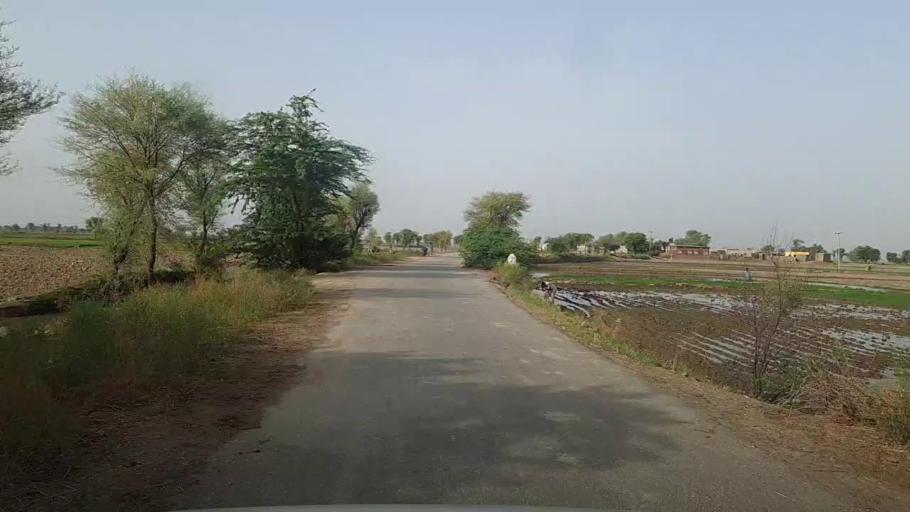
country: PK
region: Sindh
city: Khairpur Nathan Shah
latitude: 27.1029
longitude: 67.7940
